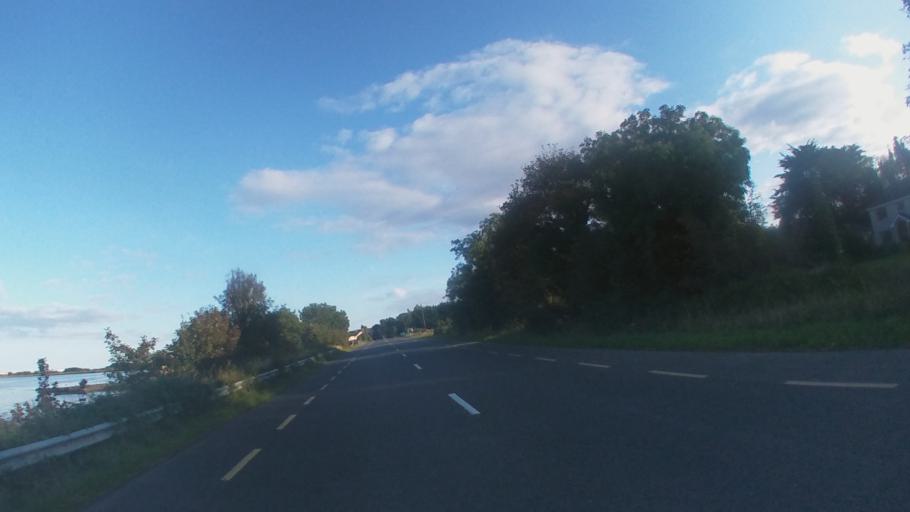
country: IE
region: Leinster
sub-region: Lu
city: Carlingford
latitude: 54.0320
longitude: -6.1593
